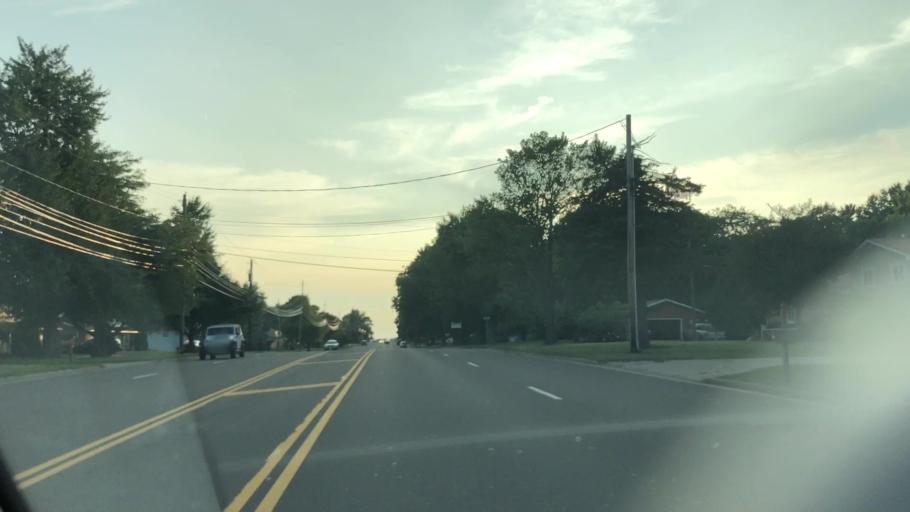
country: US
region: Ohio
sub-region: Summit County
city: Greensburg
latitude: 40.8784
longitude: -81.4680
